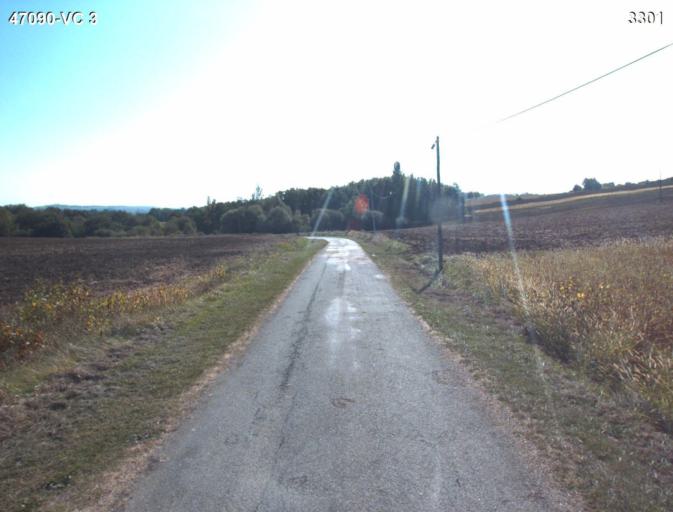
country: FR
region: Aquitaine
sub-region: Departement du Lot-et-Garonne
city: Nerac
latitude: 44.1717
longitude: 0.3810
